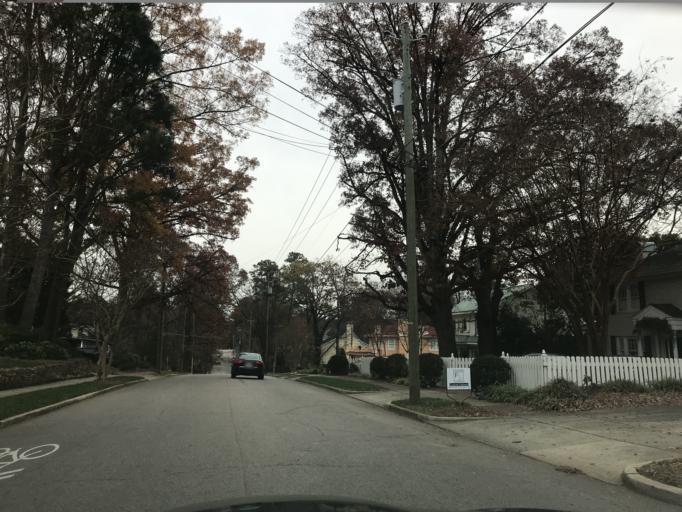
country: US
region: North Carolina
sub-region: Wake County
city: West Raleigh
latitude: 35.8009
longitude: -78.6534
